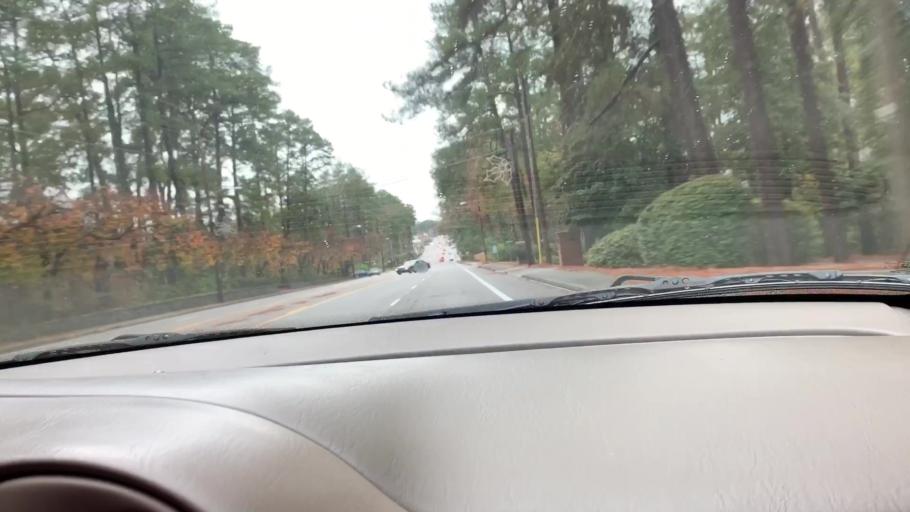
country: US
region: South Carolina
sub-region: Richland County
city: Forest Acres
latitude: 34.0245
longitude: -80.9664
